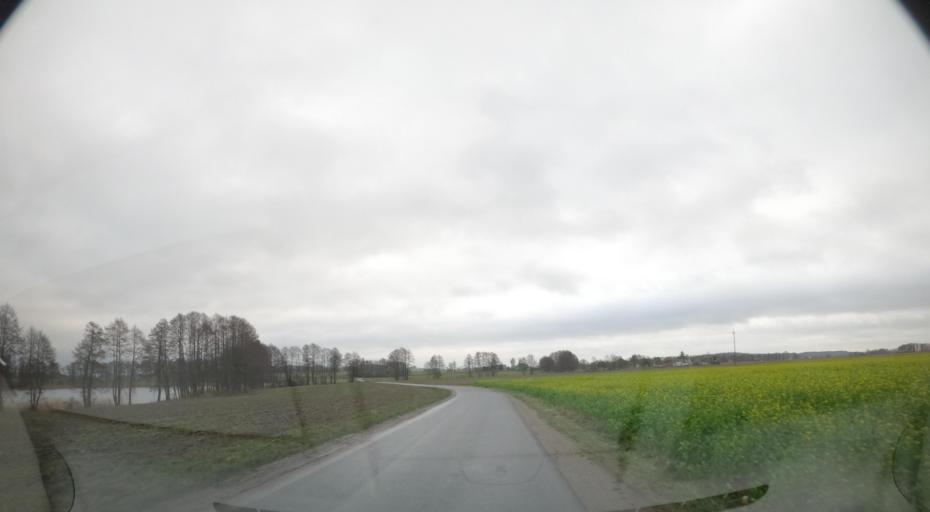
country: PL
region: Greater Poland Voivodeship
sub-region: Powiat pilski
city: Wysoka
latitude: 53.2534
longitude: 17.1433
